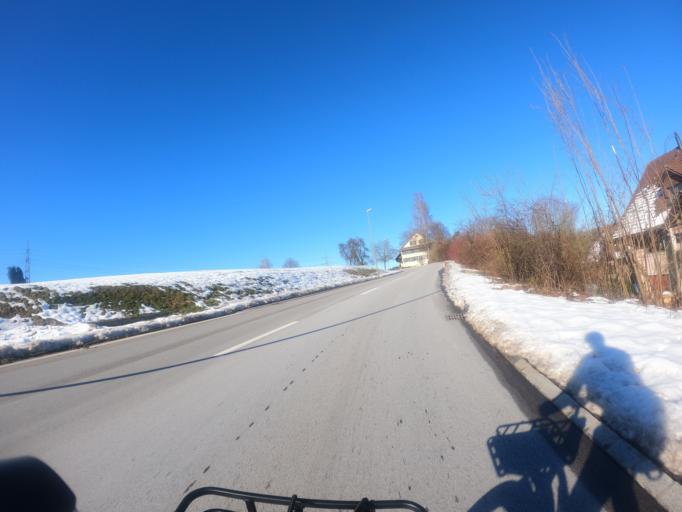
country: CH
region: Zurich
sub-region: Bezirk Affoltern
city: Hedingen
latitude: 47.2880
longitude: 8.4293
